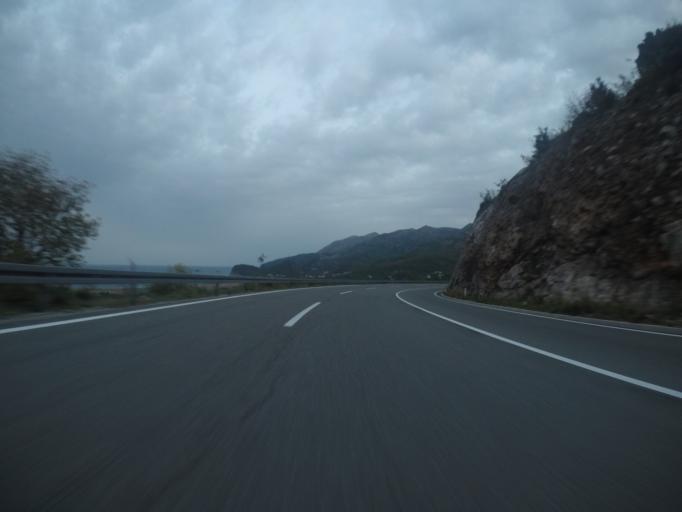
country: ME
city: Petrovac na Moru
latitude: 42.1860
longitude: 18.9891
